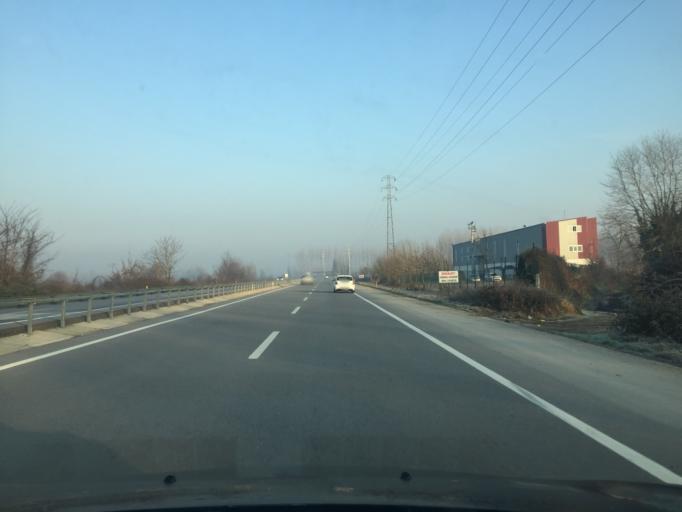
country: TR
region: Sakarya
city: Akyazi
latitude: 40.6902
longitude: 30.5741
